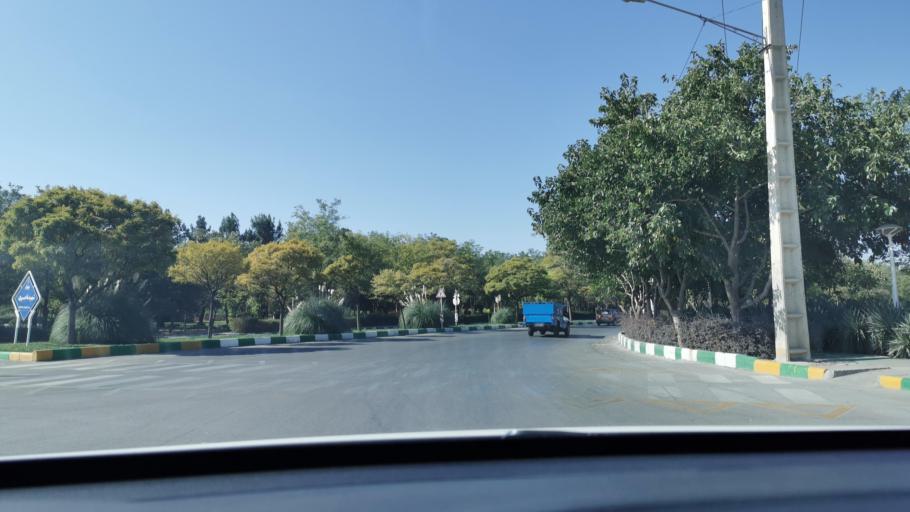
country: IR
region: Razavi Khorasan
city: Mashhad
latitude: 36.3320
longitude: 59.6425
